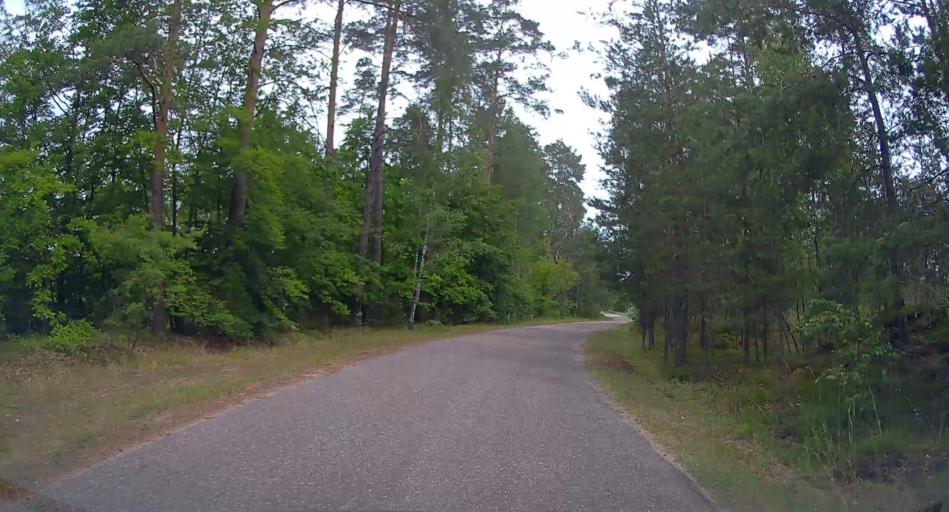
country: PL
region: Masovian Voivodeship
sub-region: Powiat ostrowski
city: Brok
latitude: 52.7383
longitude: 21.7466
